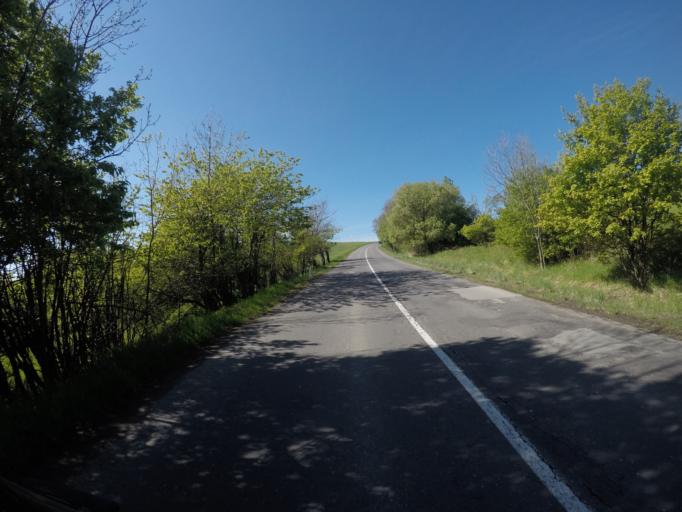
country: SK
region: Banskobystricky
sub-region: Okres Banska Bystrica
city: Banska Stiavnica
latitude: 48.4704
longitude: 18.9079
